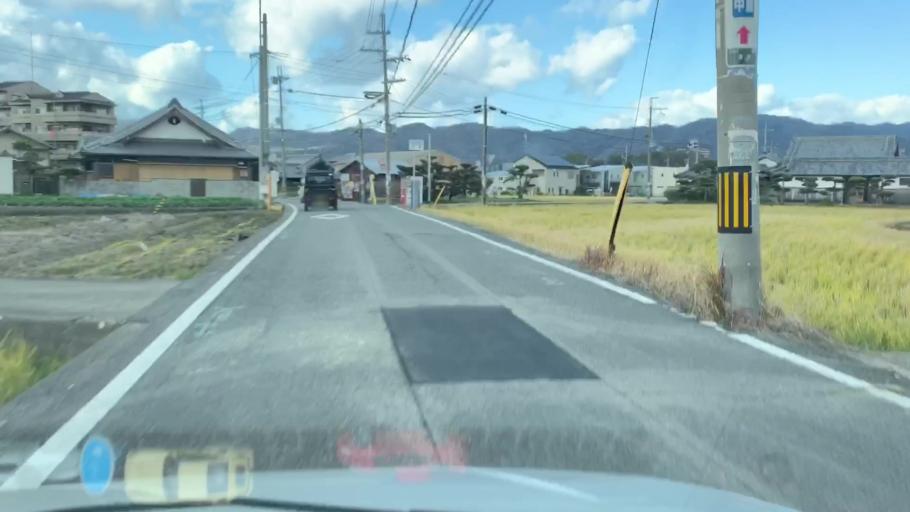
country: JP
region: Wakayama
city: Iwade
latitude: 34.2640
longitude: 135.2977
